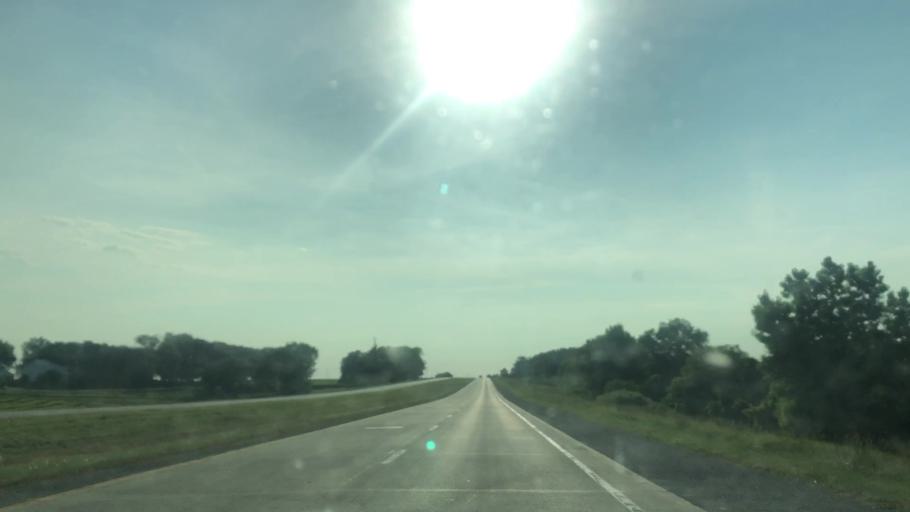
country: US
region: Iowa
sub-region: Story County
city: Nevada
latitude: 42.0077
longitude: -93.3832
